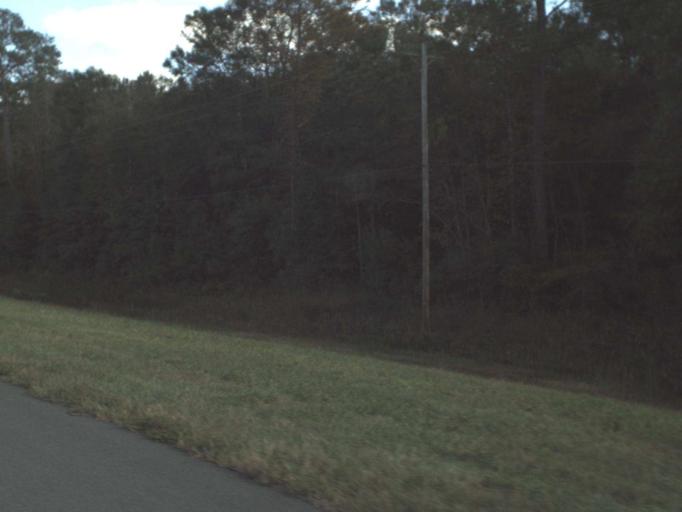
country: US
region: Florida
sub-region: Holmes County
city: Bonifay
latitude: 30.7782
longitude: -85.8365
